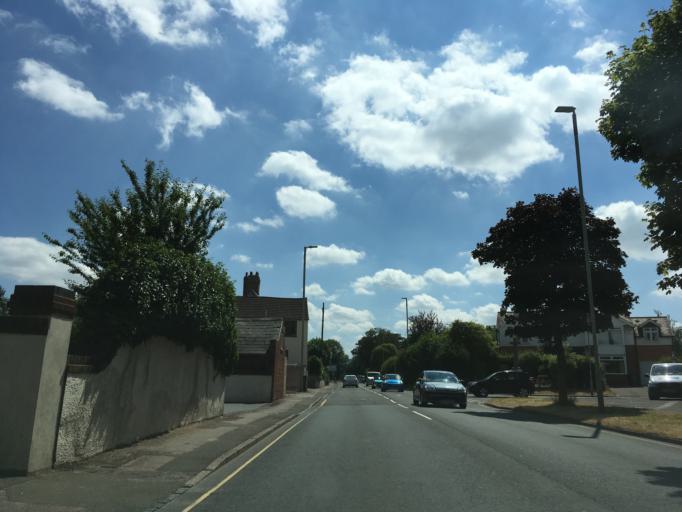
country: GB
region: England
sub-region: Gloucestershire
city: Barnwood
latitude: 51.8546
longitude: -2.1850
